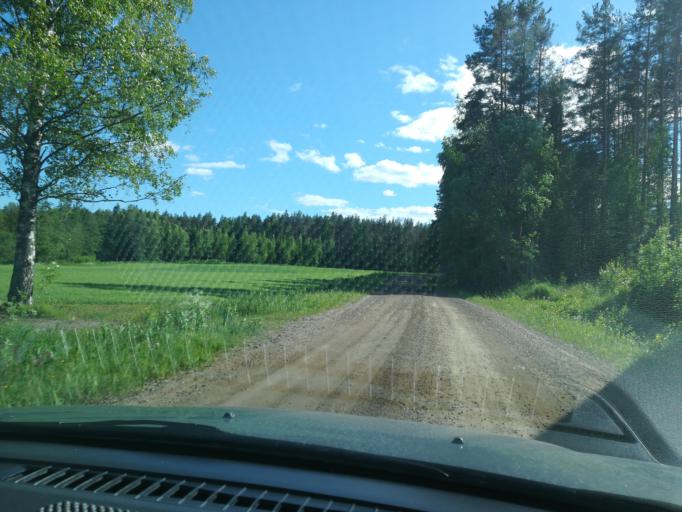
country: FI
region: Southern Savonia
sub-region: Mikkeli
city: Puumala
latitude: 61.6579
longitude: 28.1272
